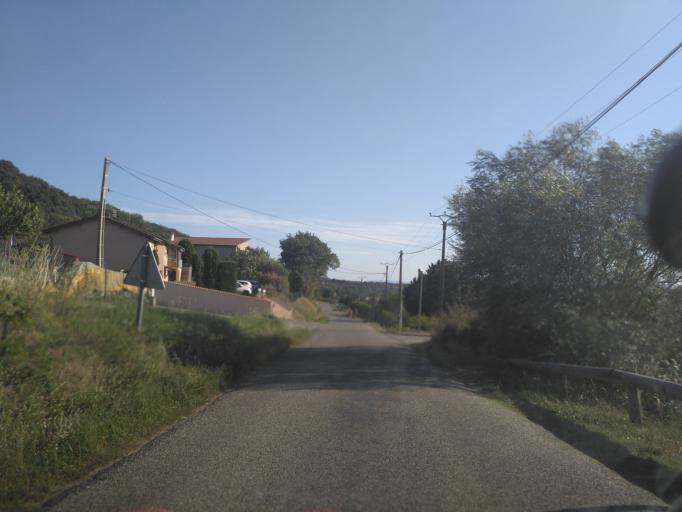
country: FR
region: Rhone-Alpes
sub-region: Departement de la Drome
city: Clerieux
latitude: 45.1329
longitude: 4.9898
